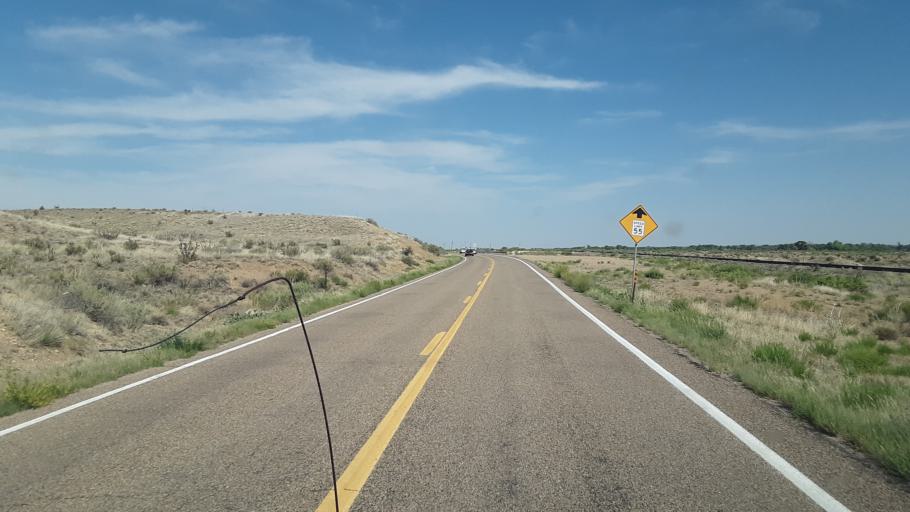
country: US
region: Colorado
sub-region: Otero County
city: Fowler
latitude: 38.1775
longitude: -104.1084
